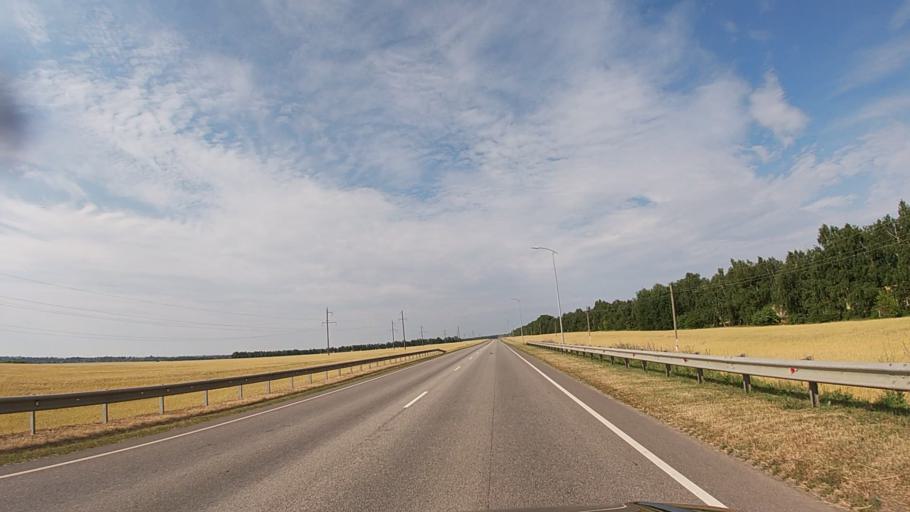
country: RU
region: Belgorod
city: Proletarskiy
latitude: 50.8211
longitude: 35.7572
